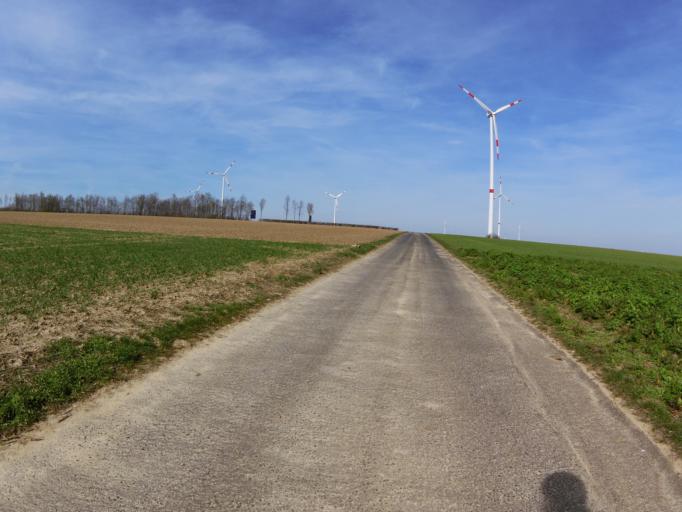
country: DE
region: Bavaria
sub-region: Regierungsbezirk Unterfranken
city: Buchbrunn
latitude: 49.7574
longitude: 10.1126
